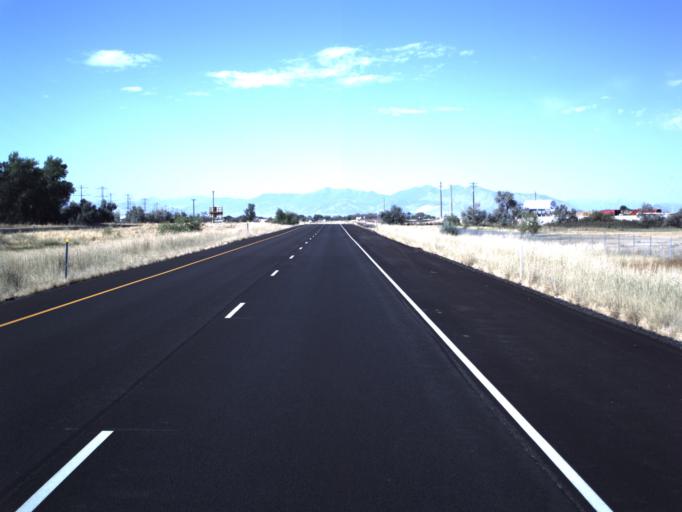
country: US
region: Utah
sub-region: Davis County
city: West Bountiful
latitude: 40.9107
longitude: -111.9135
